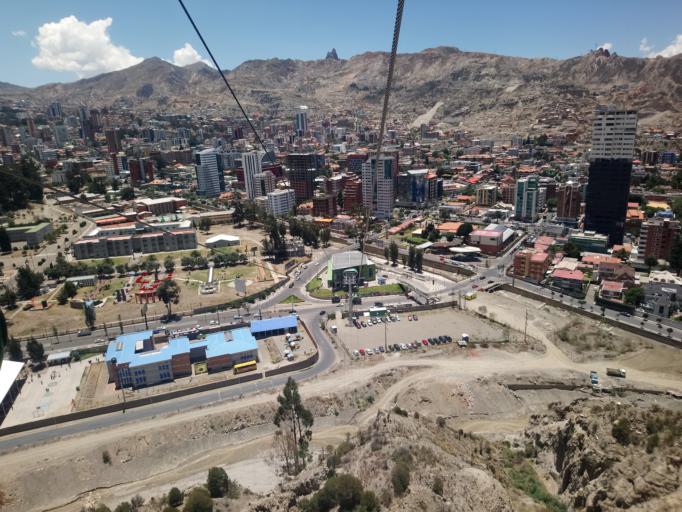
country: BO
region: La Paz
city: La Paz
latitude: -16.5365
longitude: -68.0893
